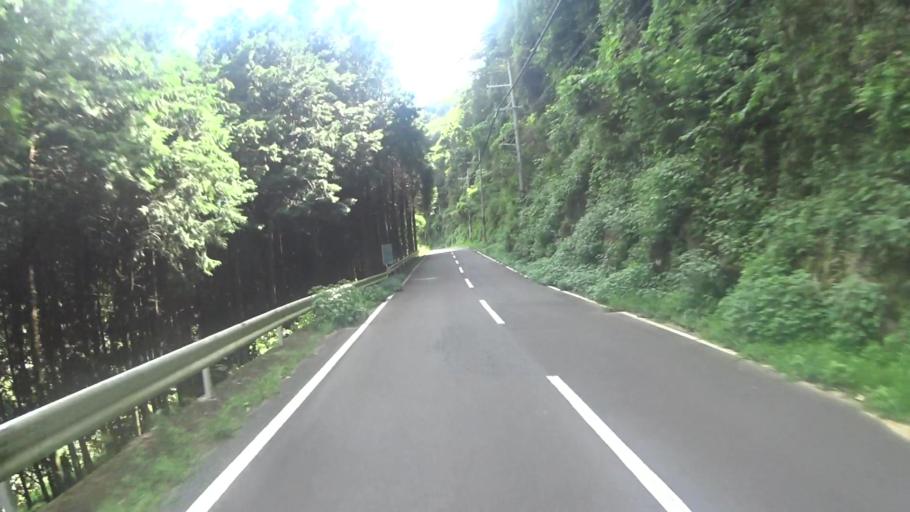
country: JP
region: Mie
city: Ueno-ebisumachi
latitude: 34.7679
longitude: 135.9937
